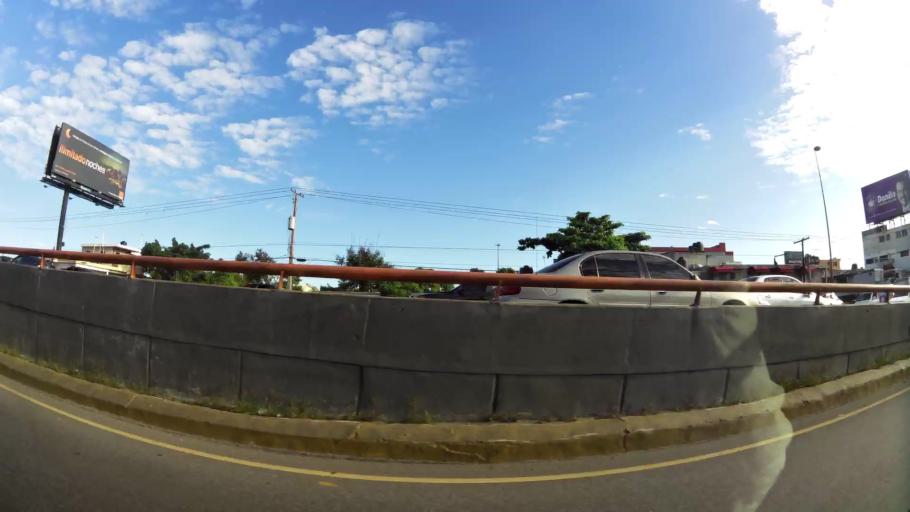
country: DO
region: Nacional
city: San Carlos
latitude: 18.4821
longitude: -69.9191
